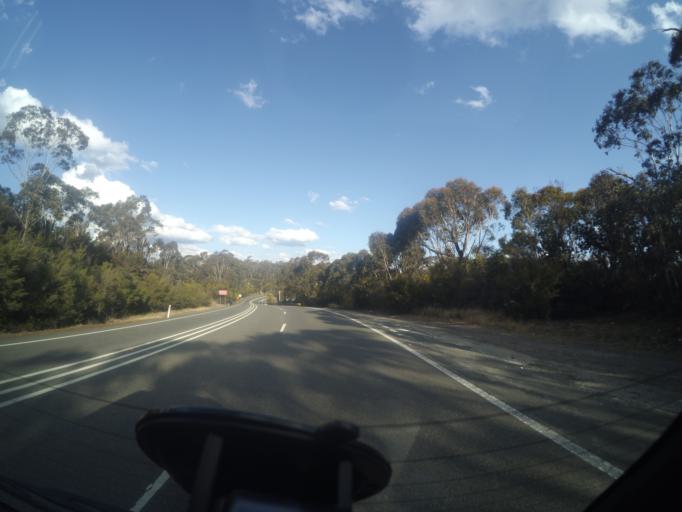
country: AU
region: New South Wales
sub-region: Blue Mountains Municipality
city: Katoomba
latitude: -33.6959
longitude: 150.2893
